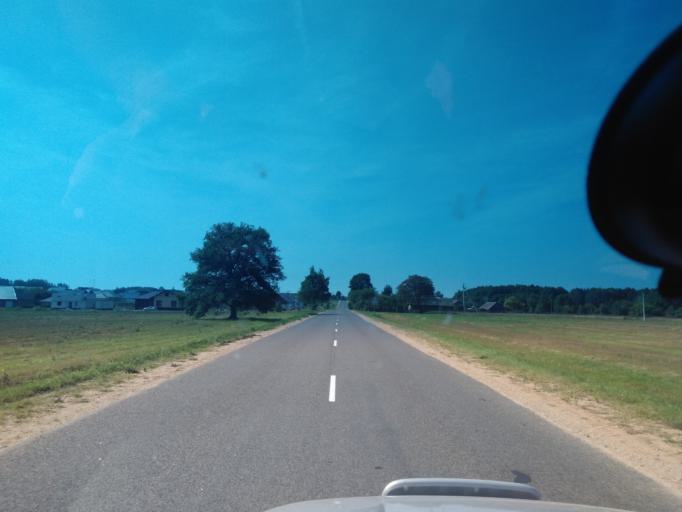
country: BY
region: Minsk
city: Kapyl'
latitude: 53.1647
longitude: 27.1041
